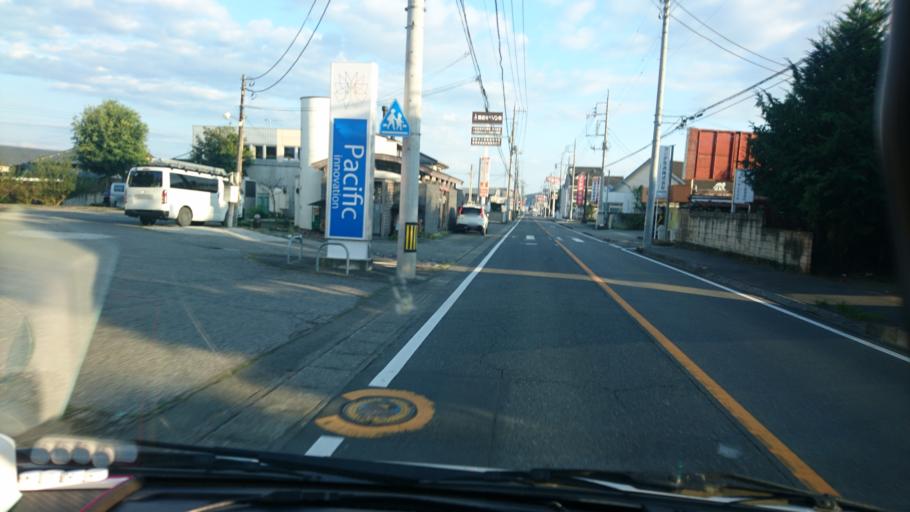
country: JP
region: Gunma
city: Kiryu
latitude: 36.3912
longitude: 139.3301
